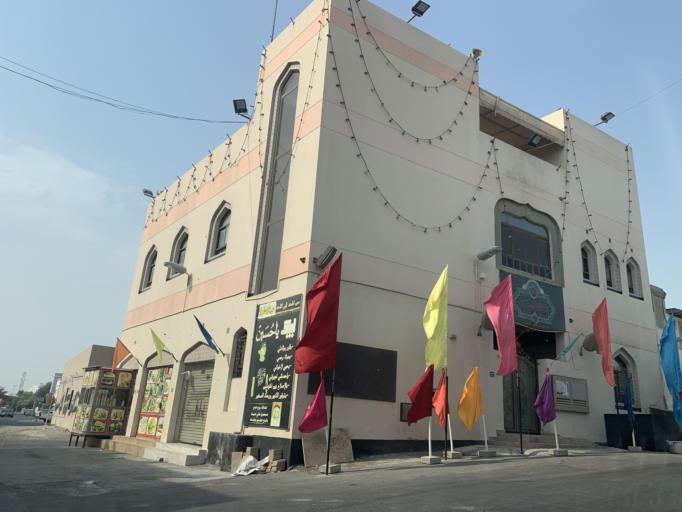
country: BH
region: Manama
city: Jidd Hafs
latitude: 26.2195
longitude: 50.4880
